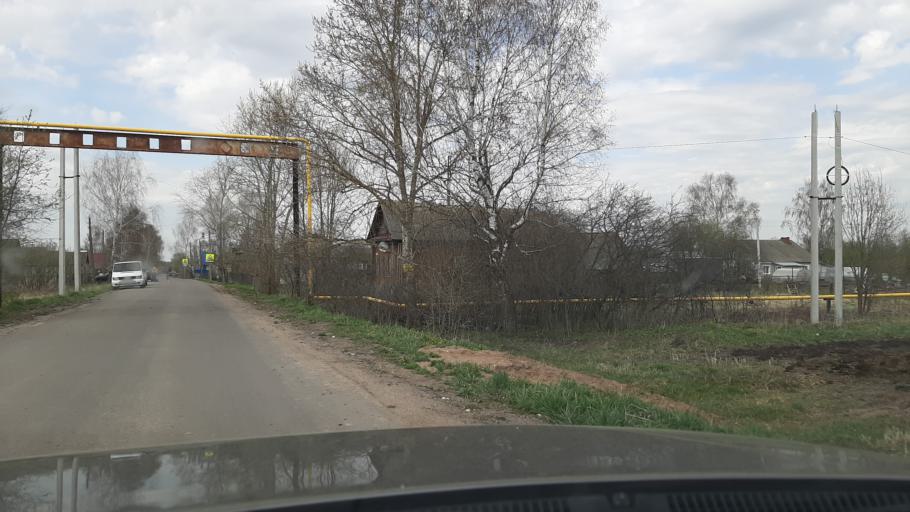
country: RU
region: Ivanovo
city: Privolzhsk
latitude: 57.3287
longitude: 41.2355
